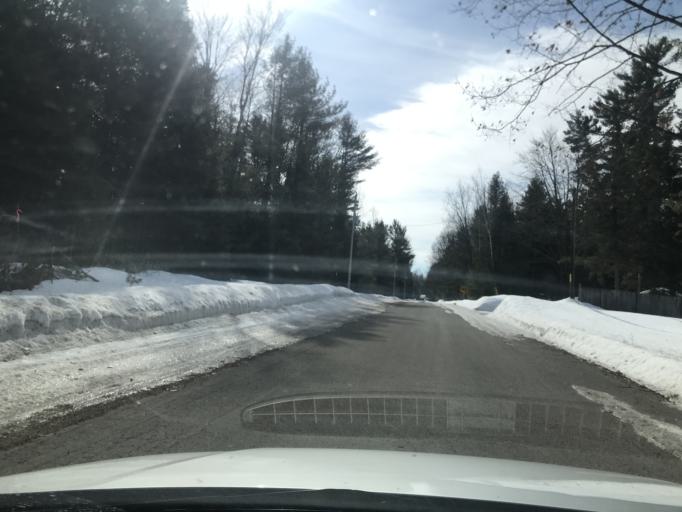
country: US
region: Wisconsin
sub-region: Menominee County
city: Legend Lake
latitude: 45.1088
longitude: -88.4330
